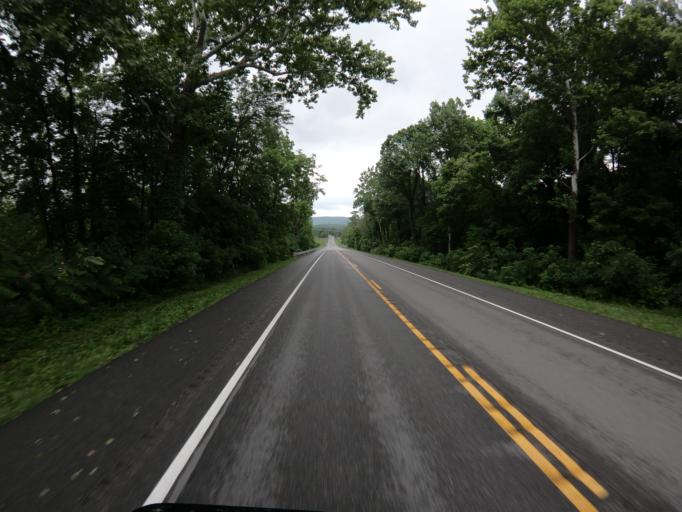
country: US
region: Maryland
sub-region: Washington County
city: Keedysville
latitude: 39.4981
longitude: -77.6808
